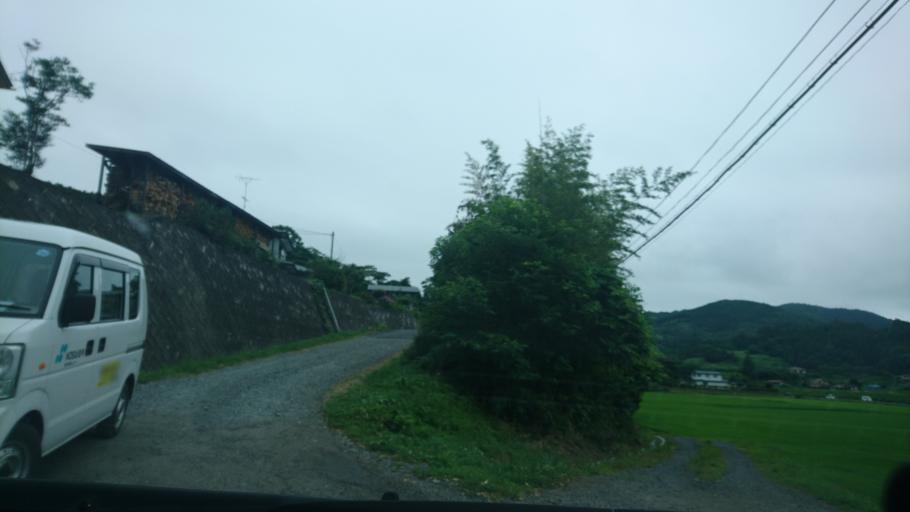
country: JP
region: Iwate
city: Ichinoseki
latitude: 38.9005
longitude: 141.2966
